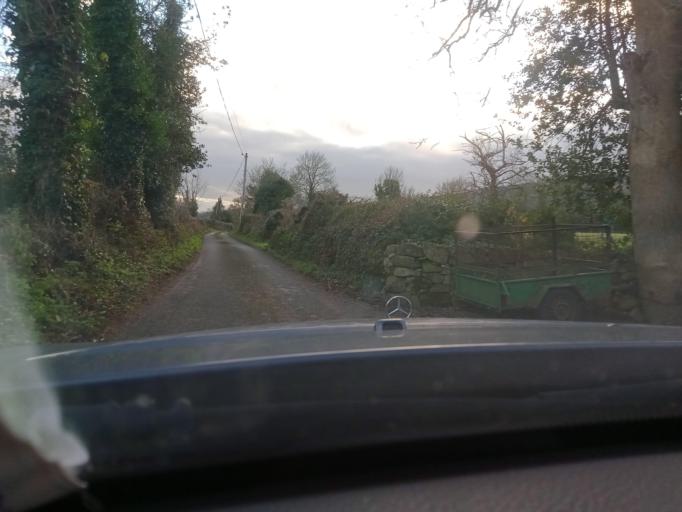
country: IE
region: Leinster
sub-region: Kilkenny
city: Graiguenamanagh
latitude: 52.5068
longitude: -6.9412
